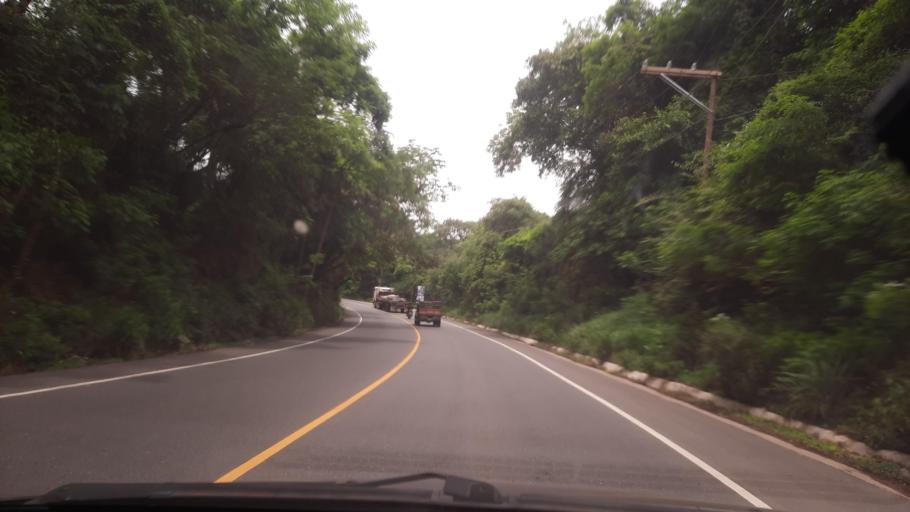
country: GT
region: Zacapa
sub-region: Municipio de Zacapa
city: Gualan
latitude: 15.1491
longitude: -89.3260
